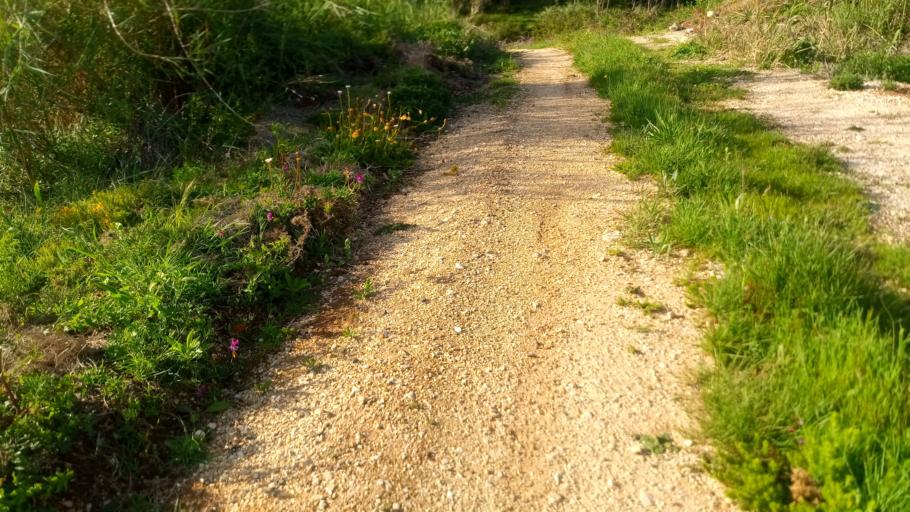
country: PT
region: Leiria
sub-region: Caldas da Rainha
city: Caldas da Rainha
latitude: 39.4563
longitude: -9.1957
